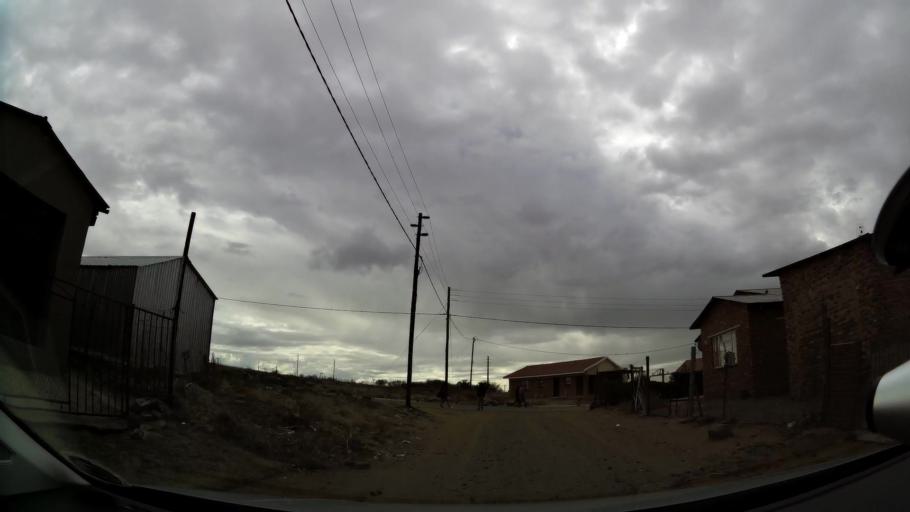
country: ZA
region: Orange Free State
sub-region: Fezile Dabi District Municipality
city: Kroonstad
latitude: -27.6471
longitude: 27.2067
